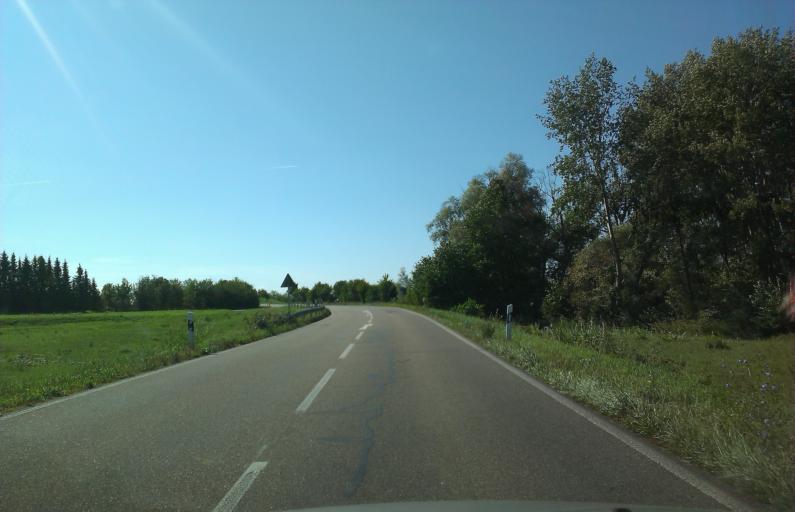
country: DE
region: Baden-Wuerttemberg
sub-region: Karlsruhe Region
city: Philippsburg
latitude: 49.2442
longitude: 8.4739
